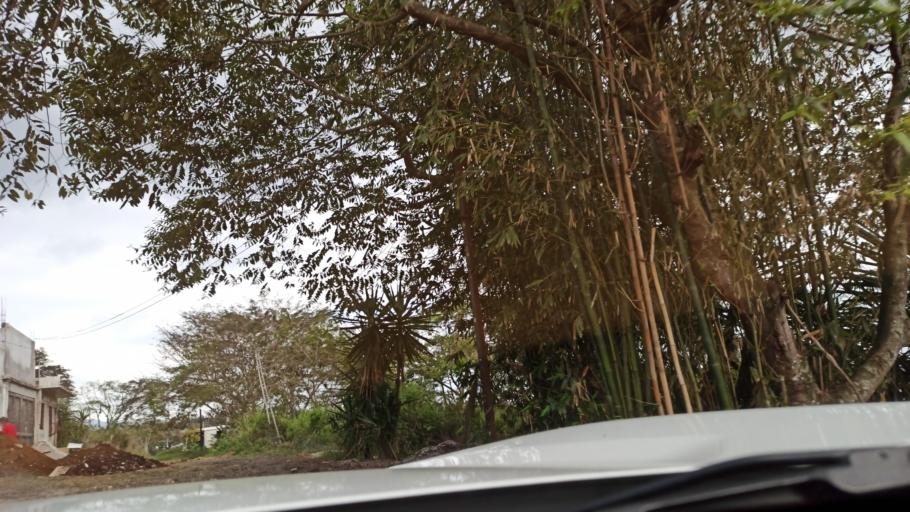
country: MX
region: Veracruz
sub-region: Fortin
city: Fortin de las Flores
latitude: 18.9151
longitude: -97.0020
